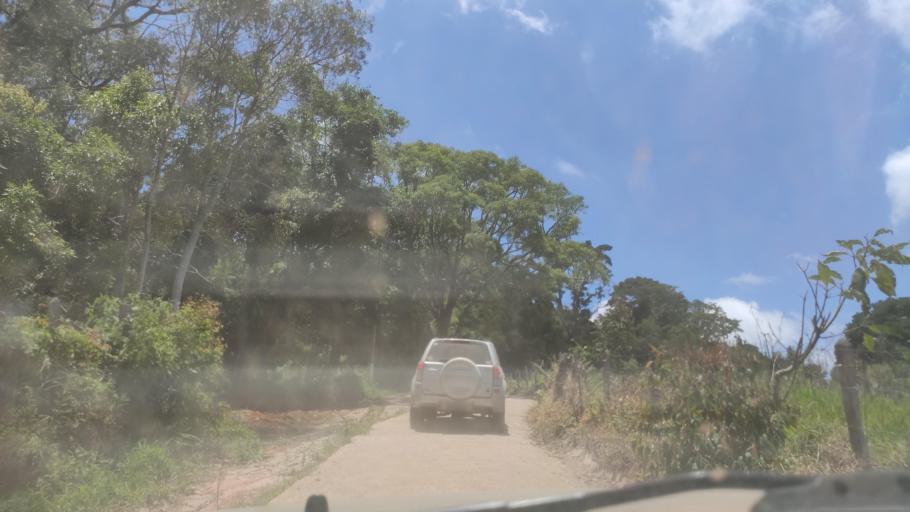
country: BR
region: Minas Gerais
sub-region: Cambui
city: Cambui
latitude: -22.6769
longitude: -45.9666
